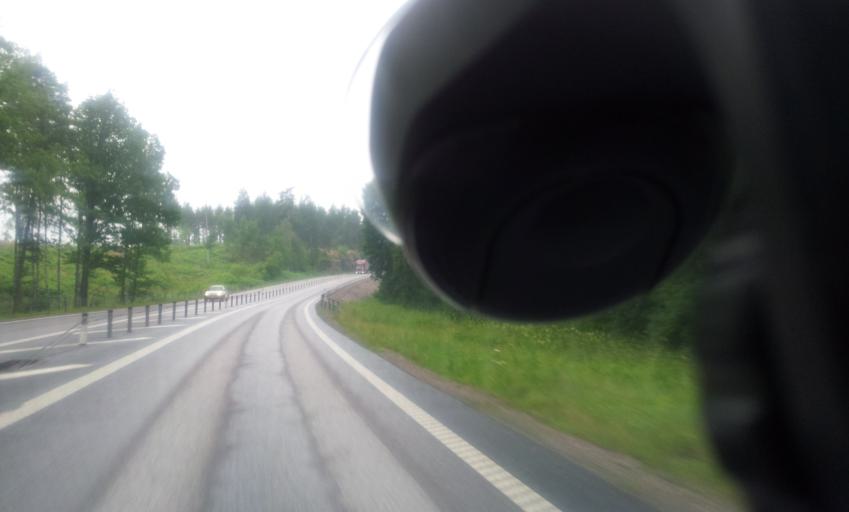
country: SE
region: Kalmar
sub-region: Vasterviks Kommun
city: Gamleby
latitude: 57.9162
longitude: 16.3995
